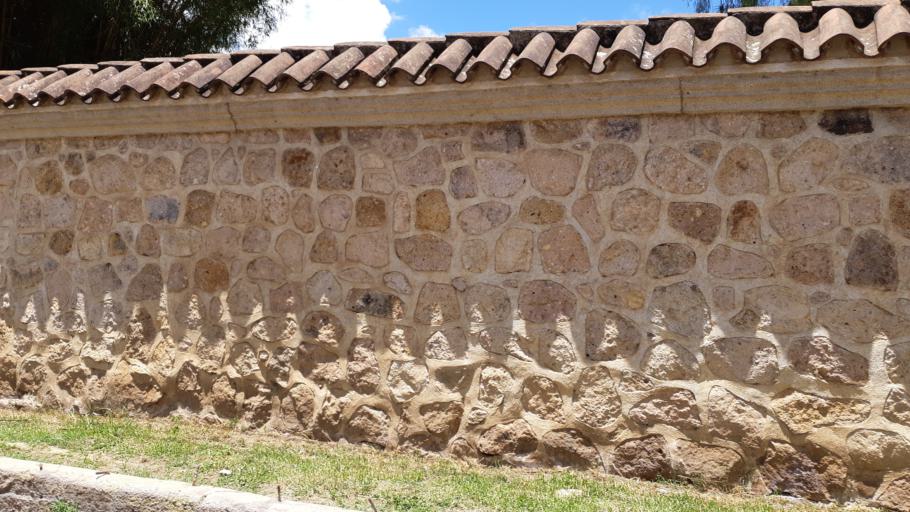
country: GT
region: Chimaltenango
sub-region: Municipio de Chimaltenango
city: Chimaltenango
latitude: 14.6631
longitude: -90.8433
